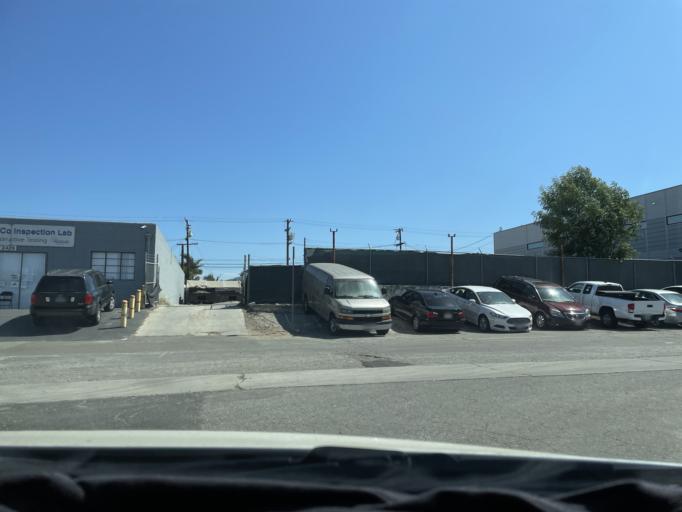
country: US
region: California
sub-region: Los Angeles County
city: Lomita
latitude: 33.8016
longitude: -118.3268
